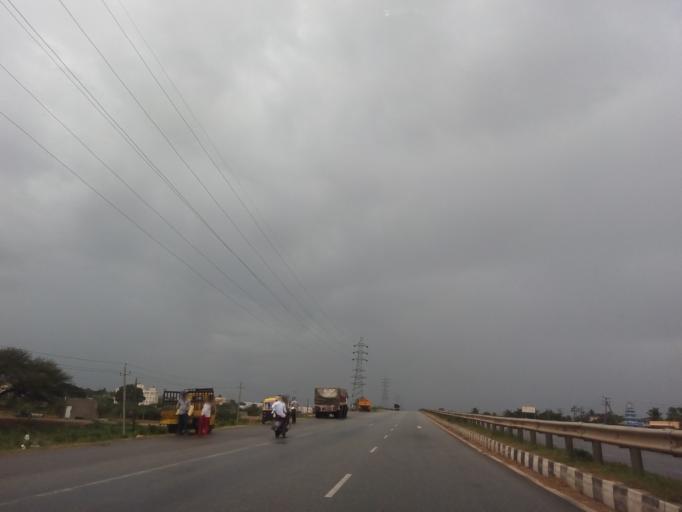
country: IN
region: Karnataka
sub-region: Davanagere
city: Harihar
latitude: 14.4427
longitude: 75.8960
